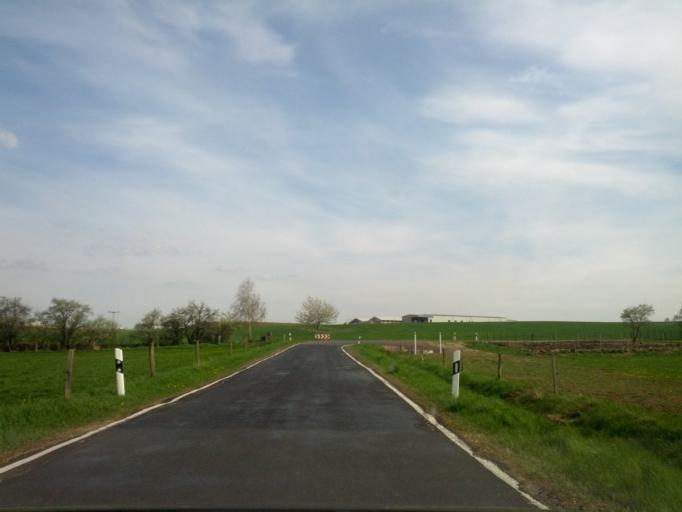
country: DE
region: Thuringia
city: Haina
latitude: 50.9650
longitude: 10.4812
